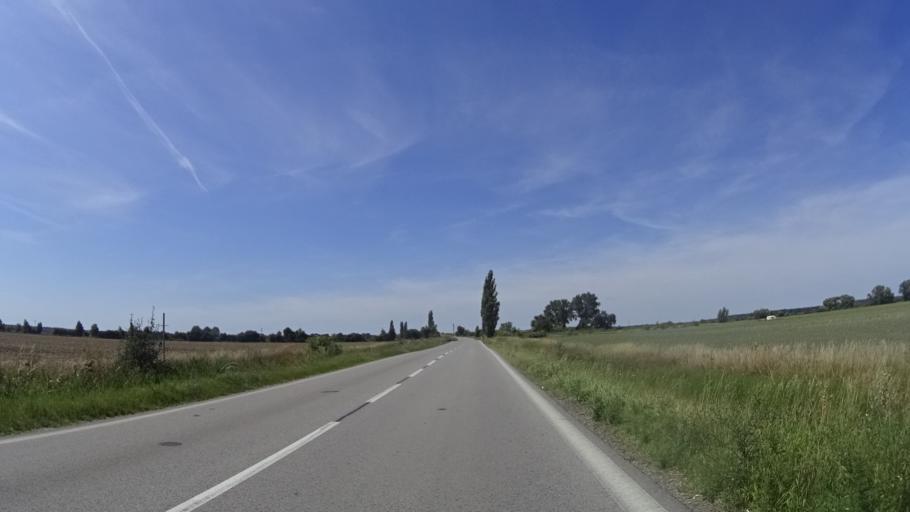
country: AT
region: Lower Austria
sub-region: Politischer Bezirk Ganserndorf
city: Marchegg
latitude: 48.3033
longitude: 16.9668
